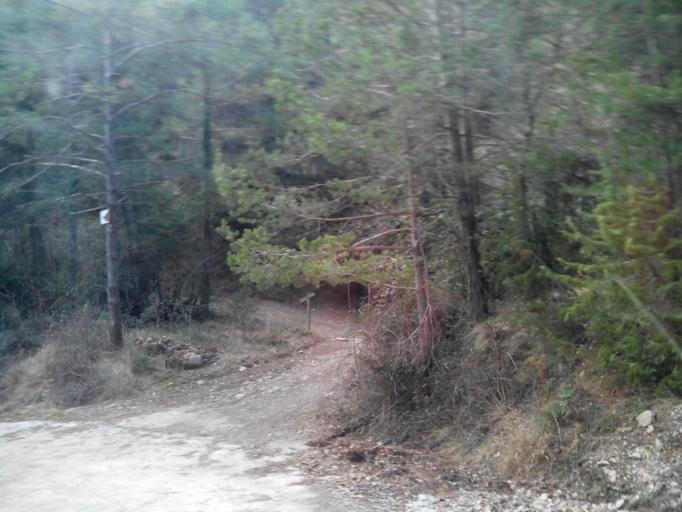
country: ES
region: Catalonia
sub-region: Provincia de Barcelona
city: Vilada
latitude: 42.1562
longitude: 1.9283
